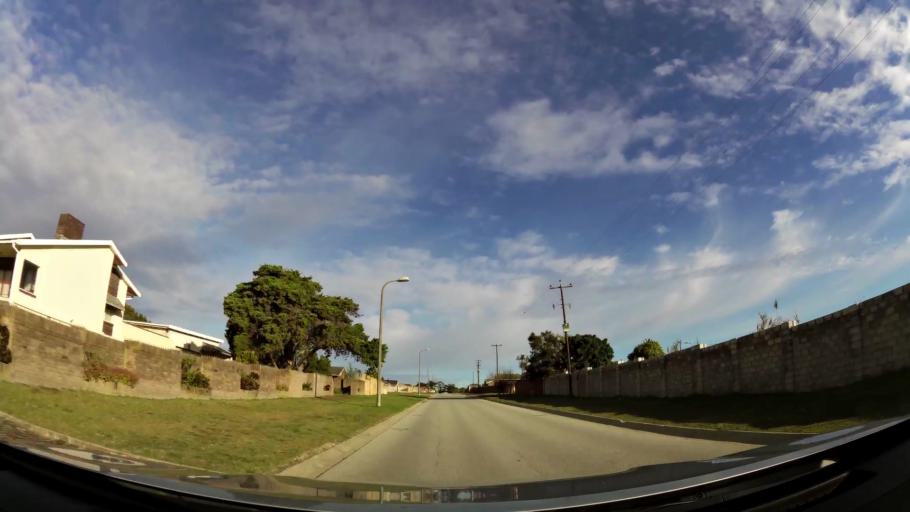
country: ZA
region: Eastern Cape
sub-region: Nelson Mandela Bay Metropolitan Municipality
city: Port Elizabeth
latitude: -33.9556
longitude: 25.4878
